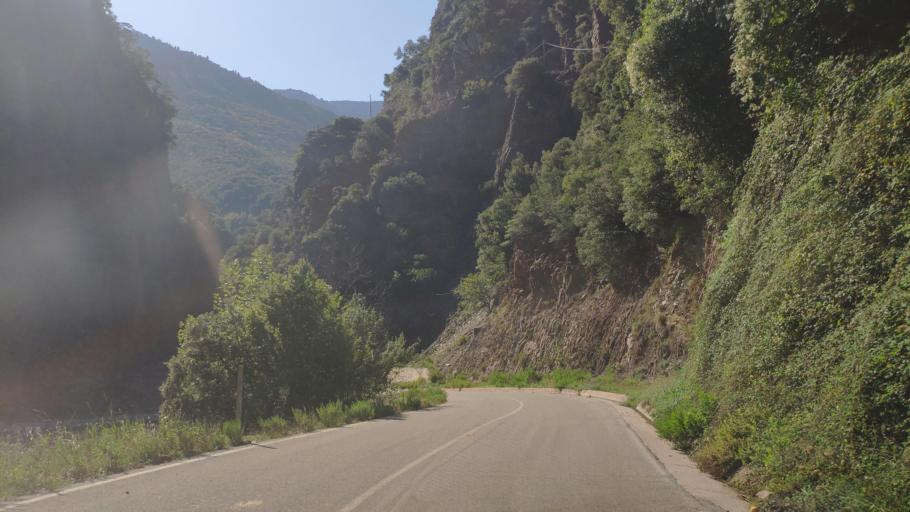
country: GR
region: Central Greece
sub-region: Nomos Evrytanias
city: Kerasochori
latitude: 39.0805
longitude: 21.5963
